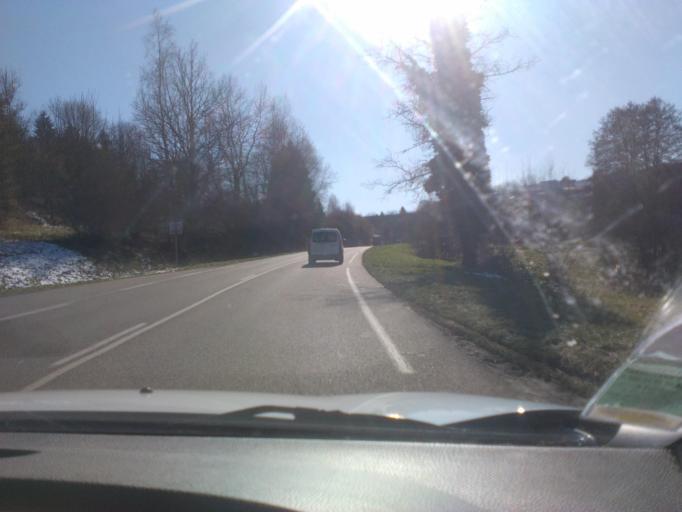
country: FR
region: Alsace
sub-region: Departement du Bas-Rhin
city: Rothau
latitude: 48.3667
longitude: 7.1383
